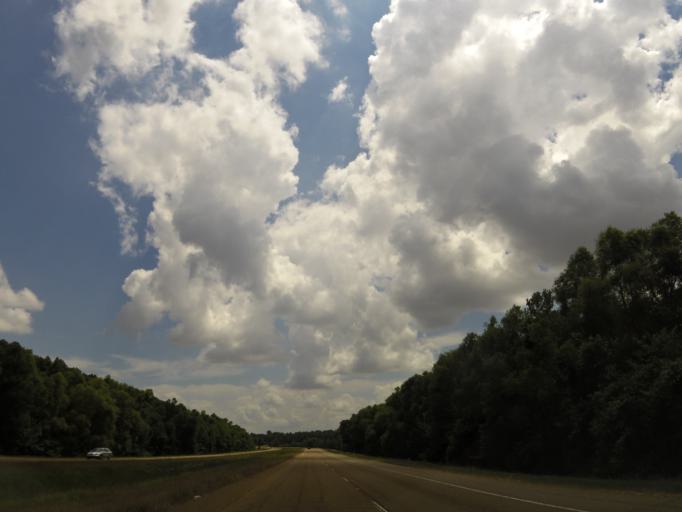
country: US
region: Tennessee
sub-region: Dyer County
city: Dyersburg
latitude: 35.9877
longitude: -89.3427
